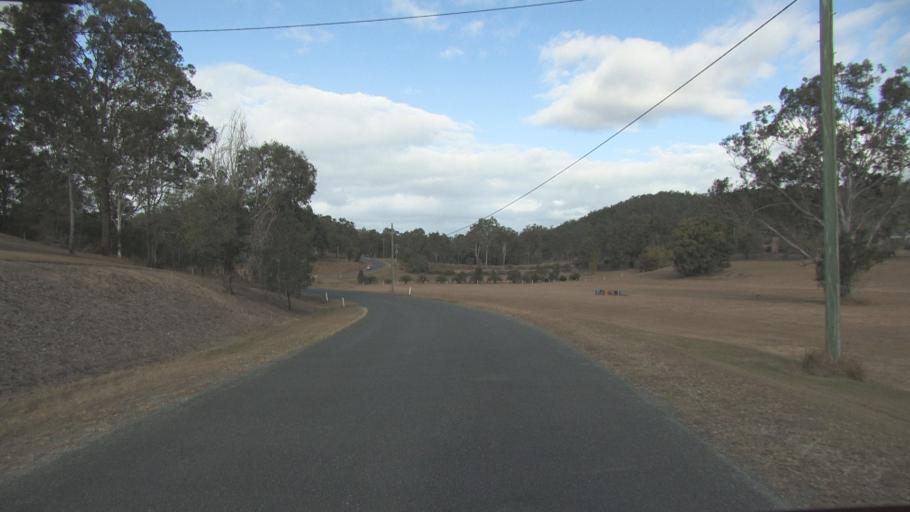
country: AU
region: Queensland
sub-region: Logan
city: Cedar Vale
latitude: -27.8999
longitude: 153.0662
